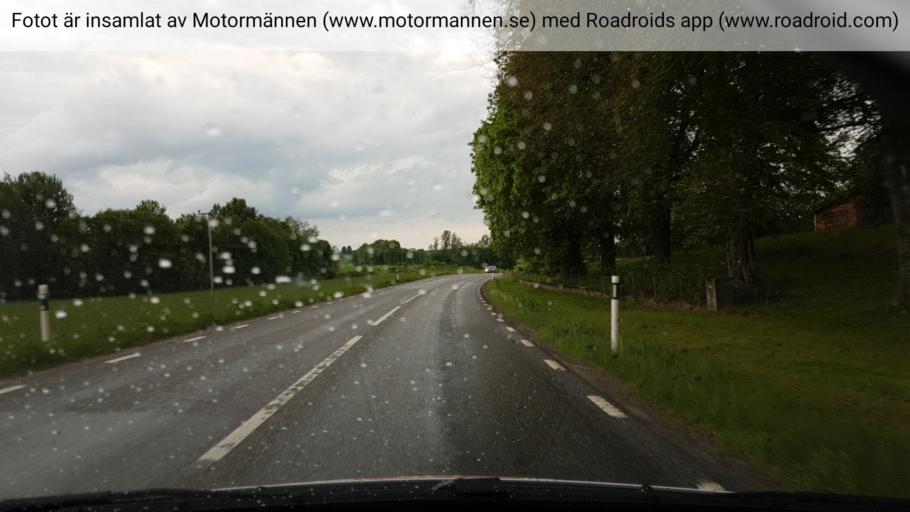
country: SE
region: OErebro
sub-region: Hallsbergs Kommun
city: Skollersta
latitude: 59.1073
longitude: 15.3263
